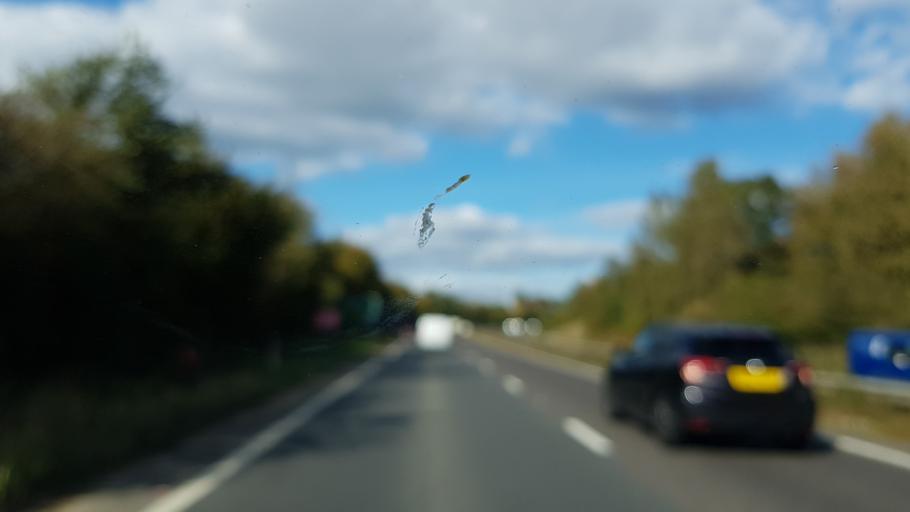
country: GB
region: England
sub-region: Surrey
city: Milford
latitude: 51.2078
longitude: -0.6508
